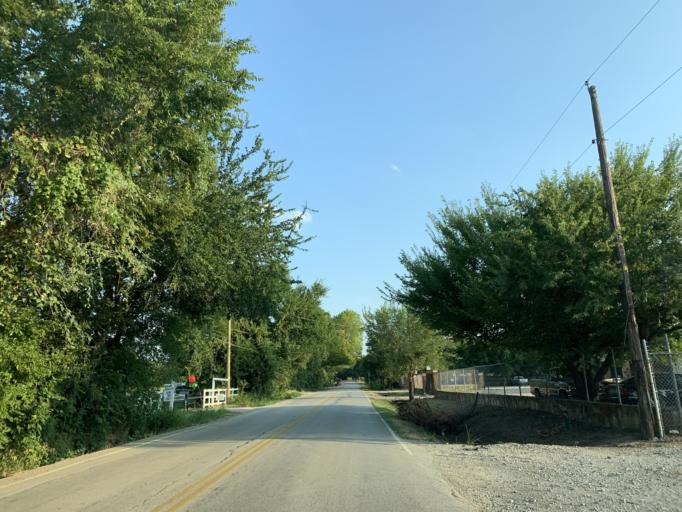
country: US
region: Texas
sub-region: Tarrant County
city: Hurst
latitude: 32.7752
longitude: -97.1750
